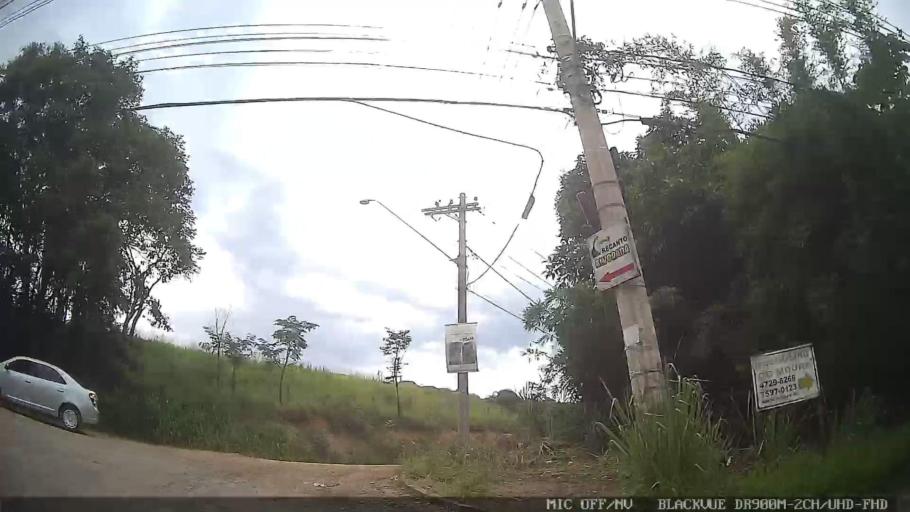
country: BR
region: Sao Paulo
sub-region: Aruja
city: Aruja
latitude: -23.4256
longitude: -46.2297
